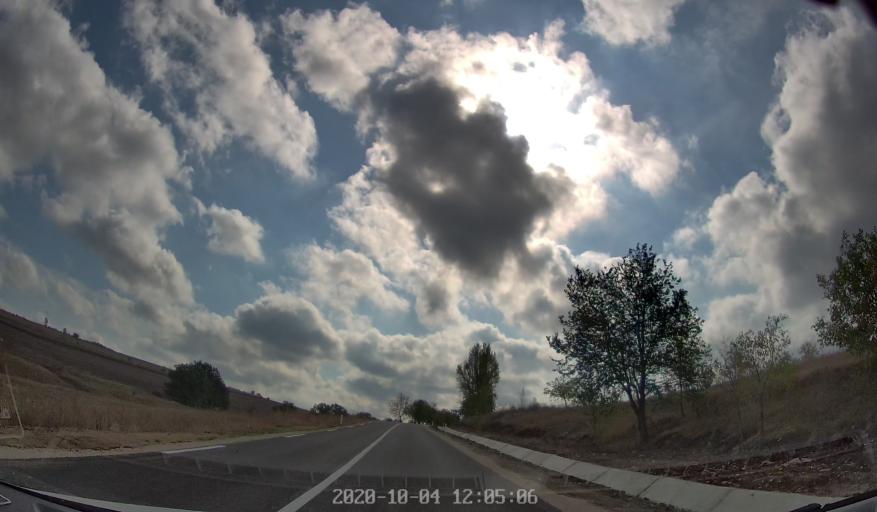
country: MD
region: Rezina
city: Saharna
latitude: 47.5971
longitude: 28.9488
